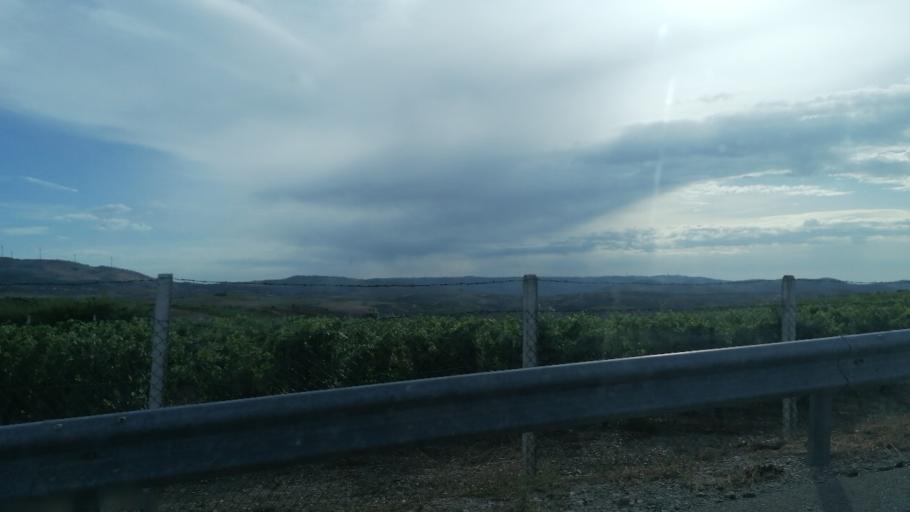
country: PT
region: Viseu
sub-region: Sao Joao da Pesqueira
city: Sao Joao da Pesqueira
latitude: 41.1048
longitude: -7.3864
